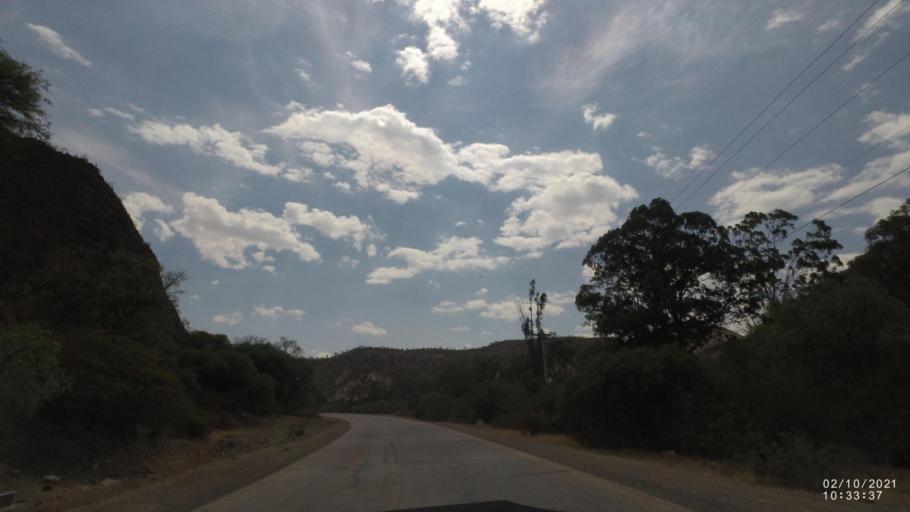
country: BO
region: Cochabamba
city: Capinota
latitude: -17.6801
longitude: -66.2515
